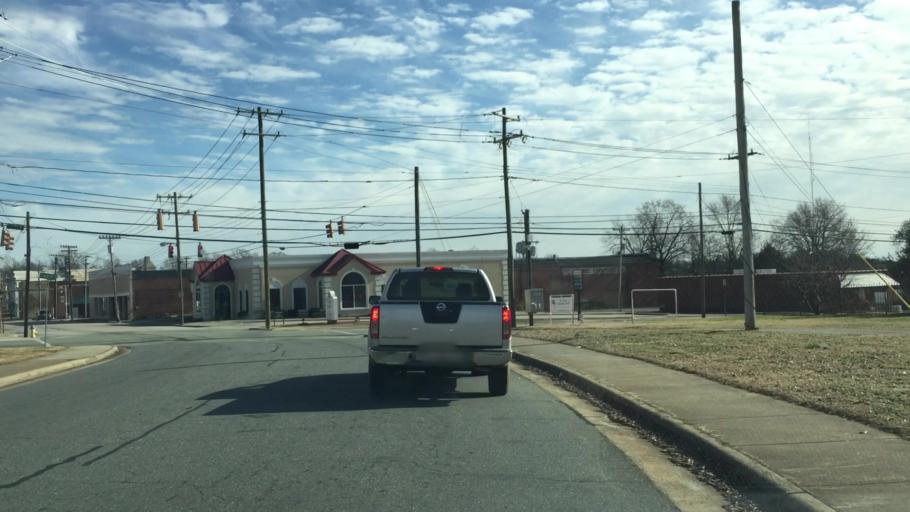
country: US
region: North Carolina
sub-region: Rockingham County
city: Reidsville
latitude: 36.3590
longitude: -79.6664
